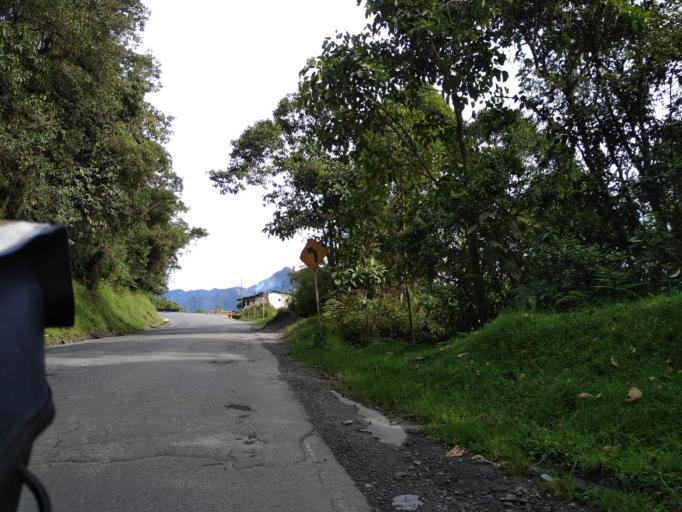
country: CO
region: Tolima
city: Herveo
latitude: 5.1246
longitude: -75.2020
